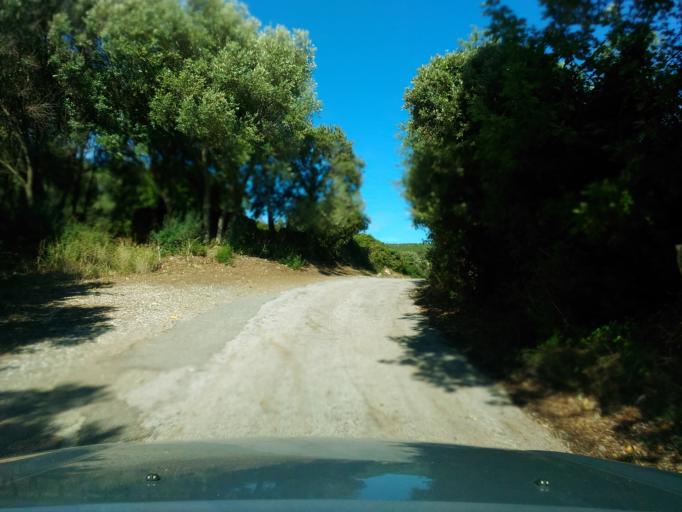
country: FR
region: Corsica
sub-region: Departement de la Haute-Corse
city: Brando
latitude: 42.9616
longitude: 9.4483
